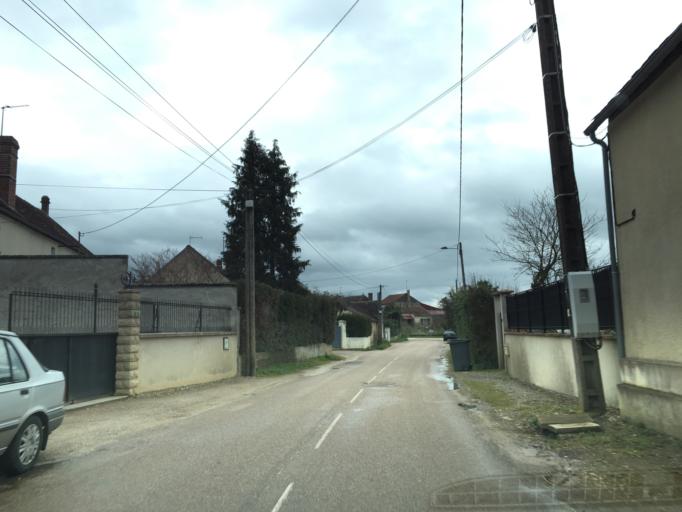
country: FR
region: Bourgogne
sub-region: Departement de l'Yonne
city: Pourrain
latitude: 47.8071
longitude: 3.3678
